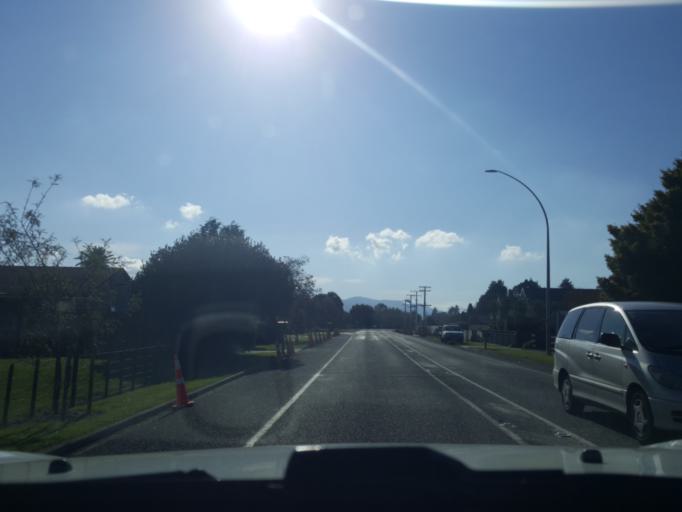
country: NZ
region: Waikato
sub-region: Waikato District
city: Ngaruawahia
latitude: -37.7375
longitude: 175.1542
